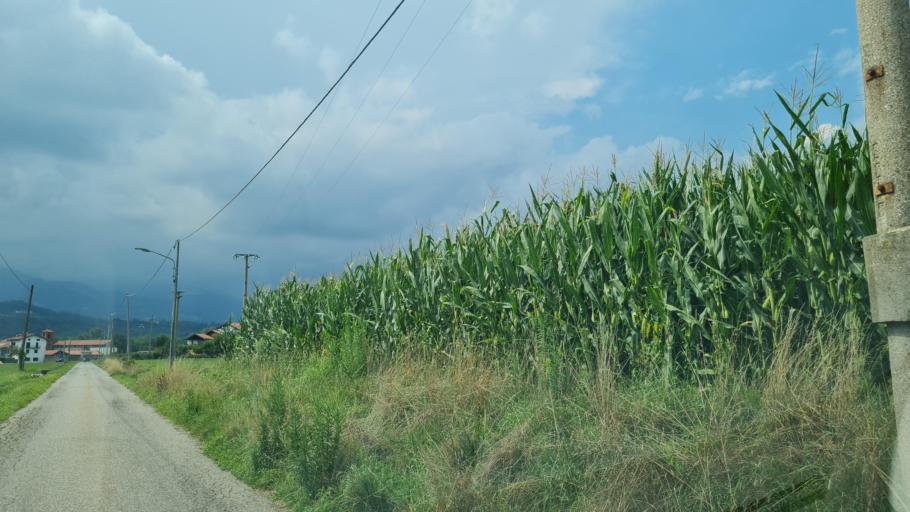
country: IT
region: Piedmont
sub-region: Provincia di Biella
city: Occhieppo Inferiore
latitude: 45.5415
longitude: 8.0290
